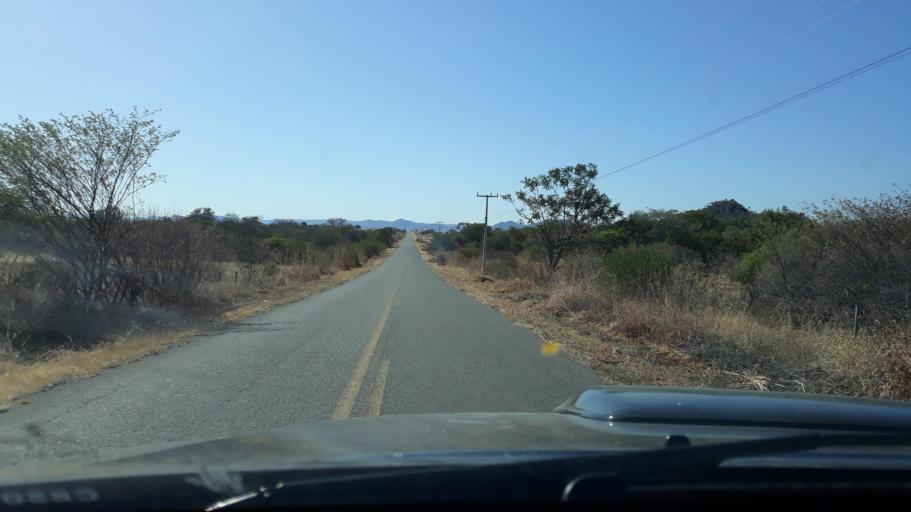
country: BR
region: Bahia
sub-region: Guanambi
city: Guanambi
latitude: -13.9854
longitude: -42.8553
